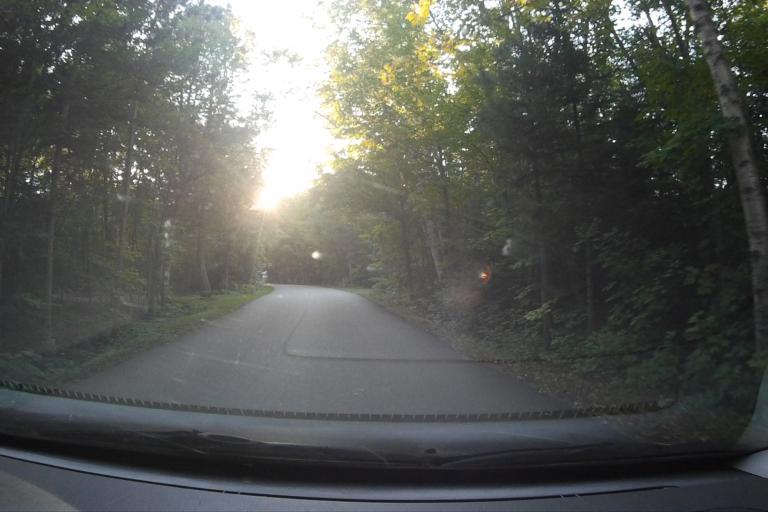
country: CA
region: Ontario
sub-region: Algoma
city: Sault Ste. Marie
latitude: 46.9697
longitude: -84.6867
